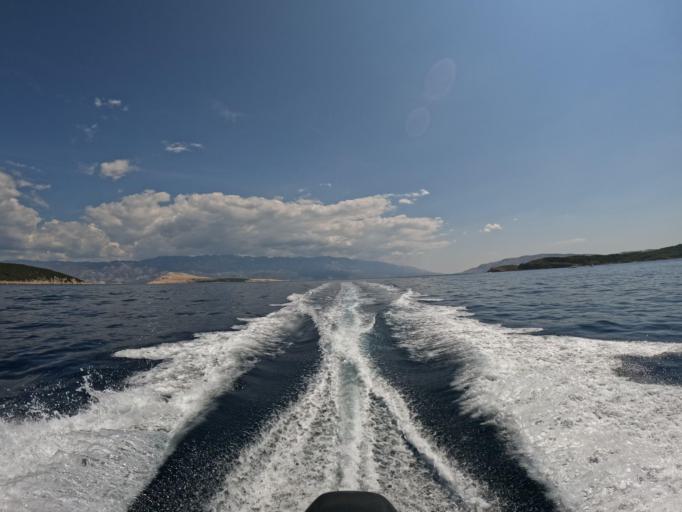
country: HR
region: Primorsko-Goranska
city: Lopar
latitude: 44.8525
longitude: 14.7553
